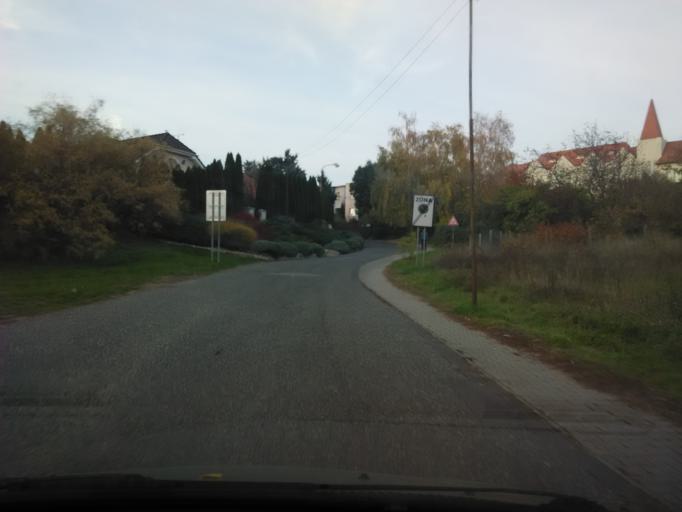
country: SK
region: Nitriansky
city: Levice
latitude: 48.2212
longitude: 18.6078
